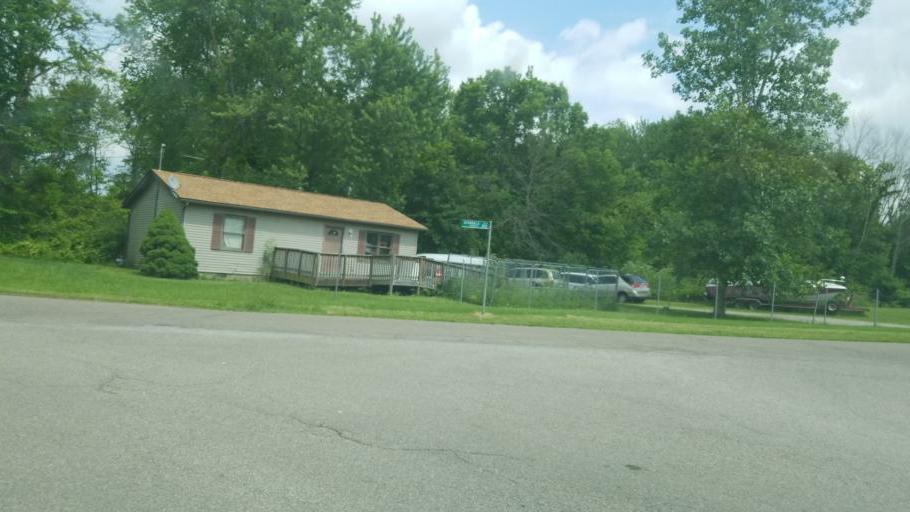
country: US
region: Ohio
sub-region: Licking County
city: Harbor Hills
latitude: 39.9353
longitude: -82.4345
